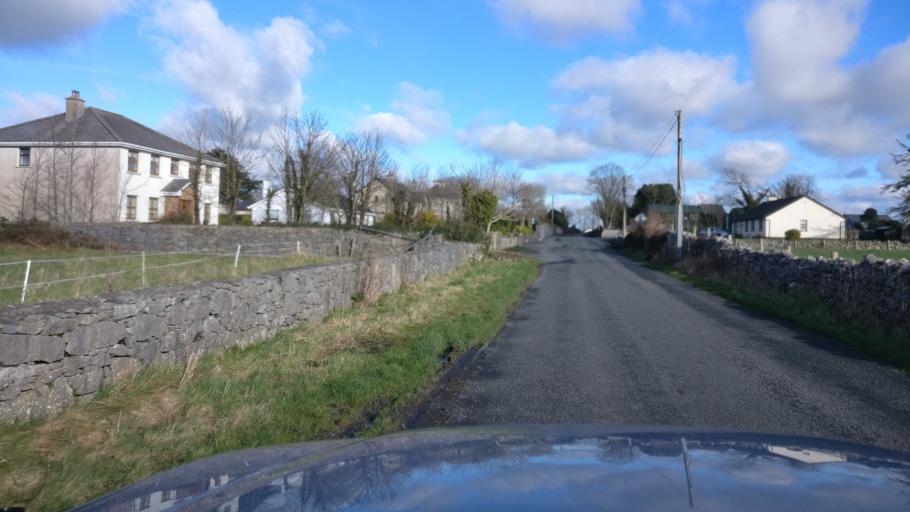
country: IE
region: Connaught
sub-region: County Galway
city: Oranmore
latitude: 53.2814
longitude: -8.8995
